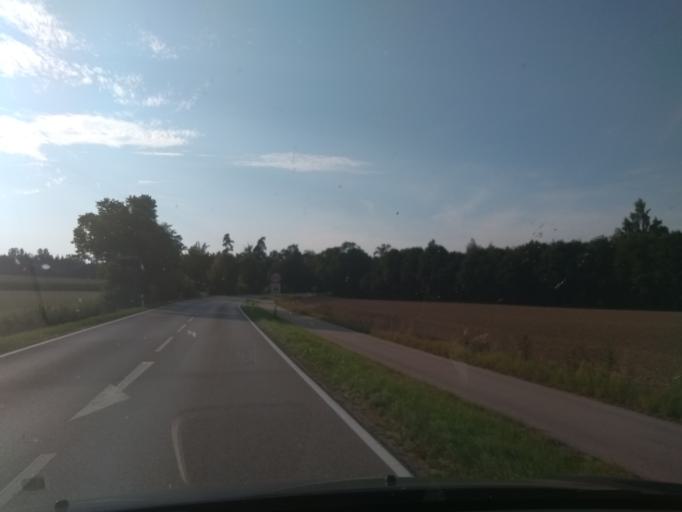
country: DE
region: Bavaria
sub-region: Upper Bavaria
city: Schwabhausen
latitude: 48.3066
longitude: 11.3913
